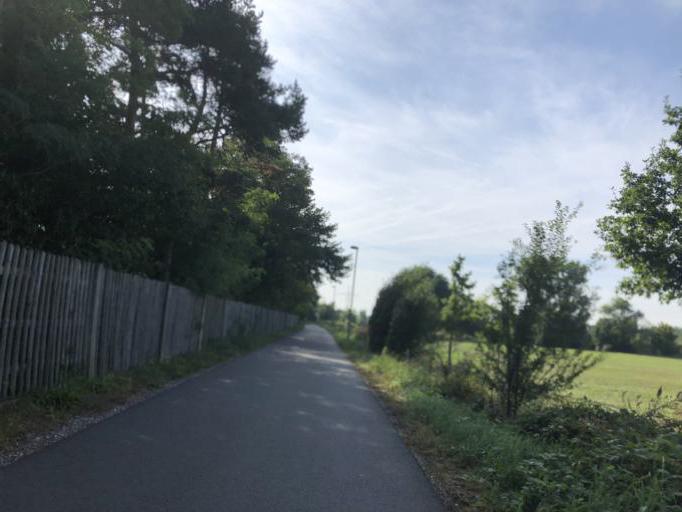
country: DE
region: Bavaria
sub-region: Regierungsbezirk Mittelfranken
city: Furth
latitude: 49.5071
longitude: 10.9757
